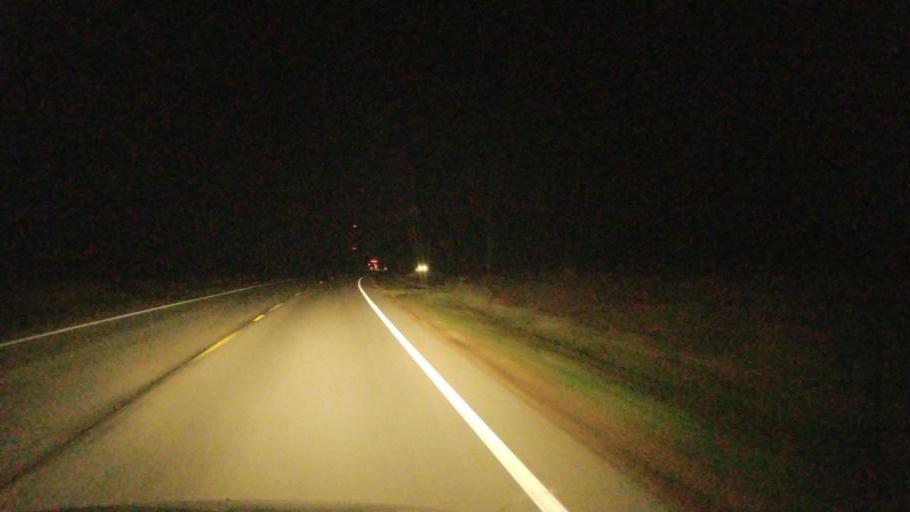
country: US
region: Ohio
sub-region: Highland County
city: Leesburg
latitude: 39.3660
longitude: -83.5518
